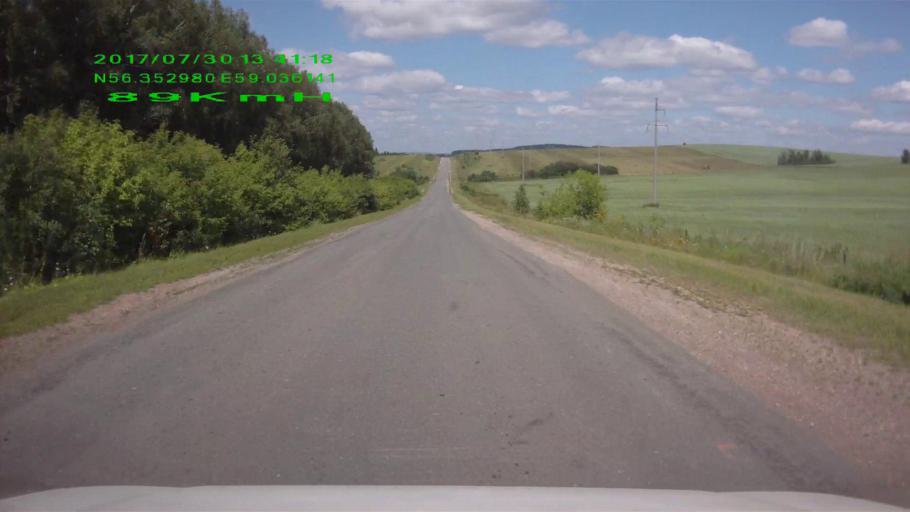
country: RU
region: Sverdlovsk
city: Mikhaylovsk
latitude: 56.3535
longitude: 59.0362
